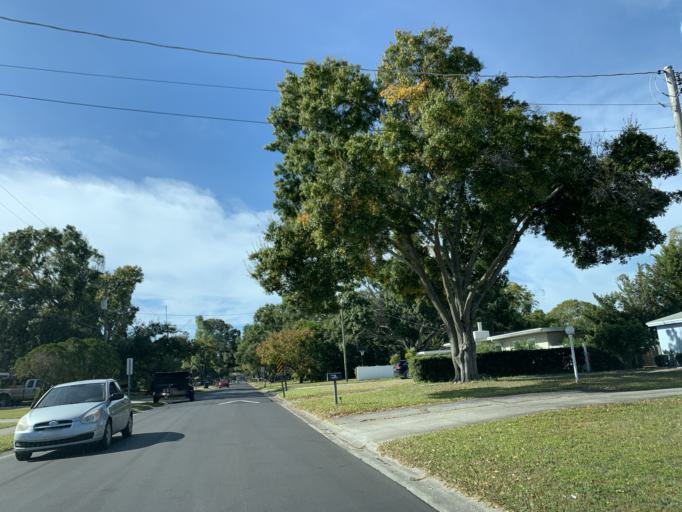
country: US
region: Florida
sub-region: Hillsborough County
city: Tampa
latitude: 27.8876
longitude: -82.5085
